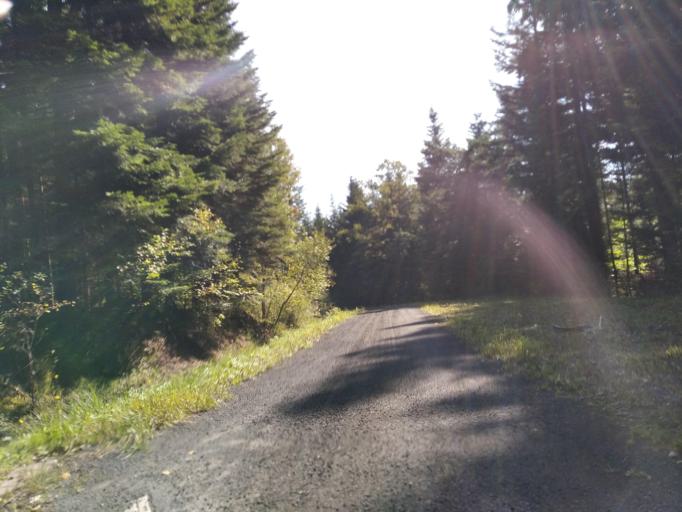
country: PL
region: Subcarpathian Voivodeship
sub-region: Powiat strzyzowski
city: Strzyzow
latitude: 49.8104
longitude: 21.8010
